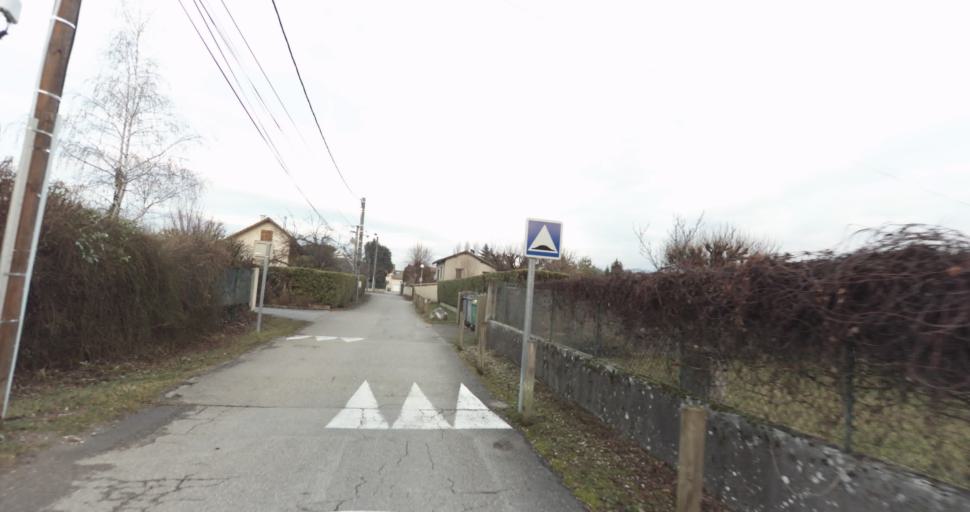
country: FR
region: Rhone-Alpes
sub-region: Departement de l'Isere
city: Vif
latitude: 45.0728
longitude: 5.6935
